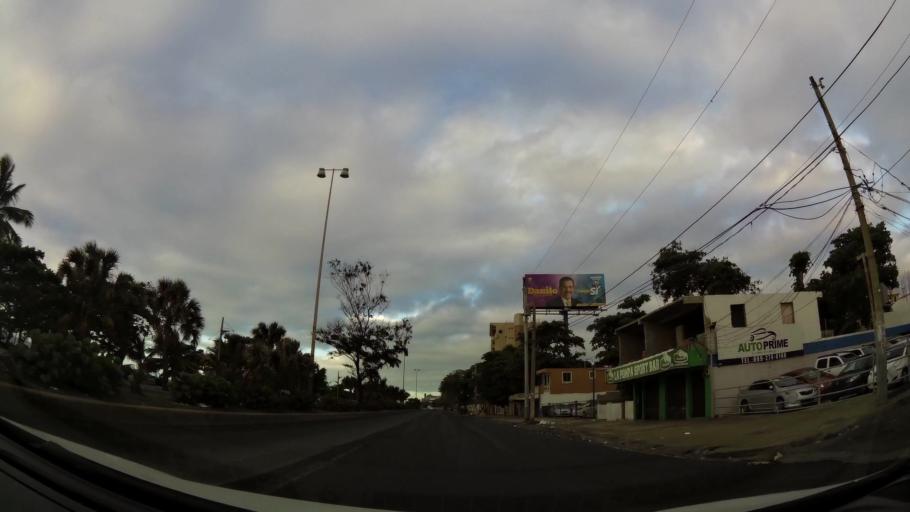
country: DO
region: Nacional
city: Bella Vista
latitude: 18.4379
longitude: -69.9373
